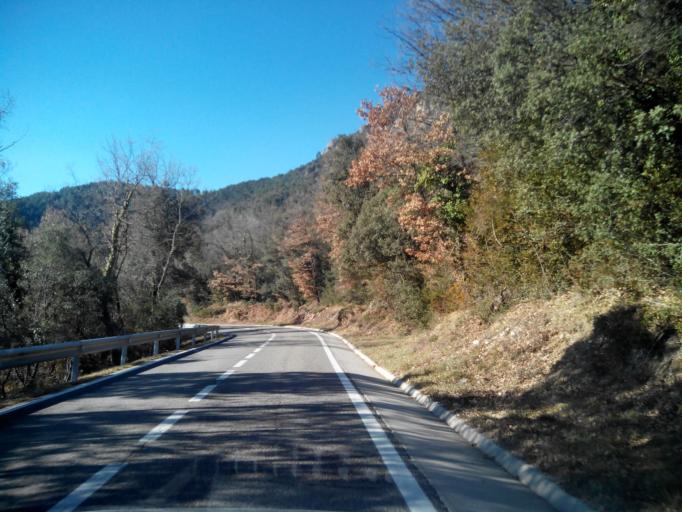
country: ES
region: Catalonia
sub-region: Provincia de Barcelona
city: Berga
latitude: 42.1005
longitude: 1.8121
